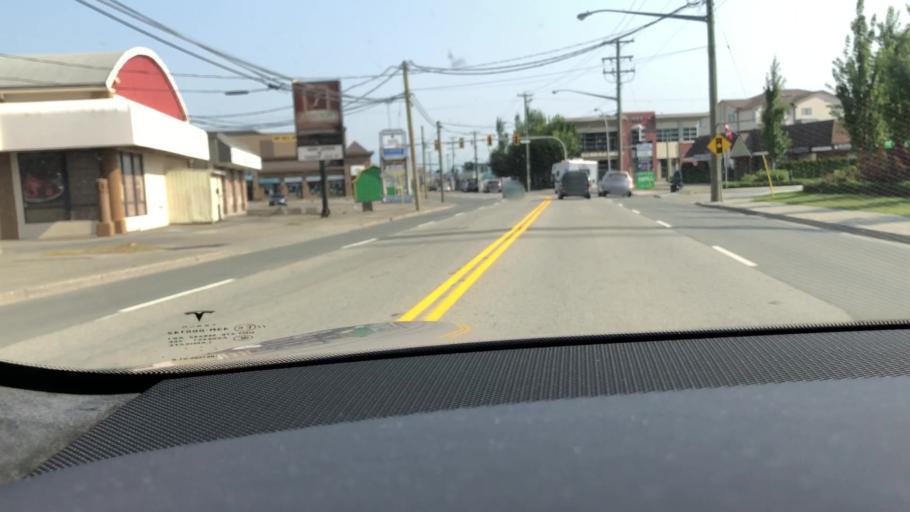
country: CA
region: British Columbia
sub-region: Fraser Valley Regional District
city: Chilliwack
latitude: 49.1354
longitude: -121.9594
